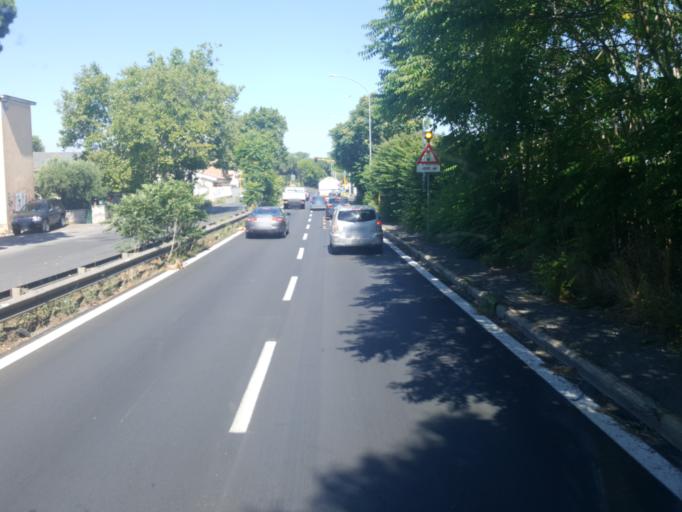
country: IT
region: Latium
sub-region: Citta metropolitana di Roma Capitale
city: Ciampino
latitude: 41.8268
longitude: 12.6271
